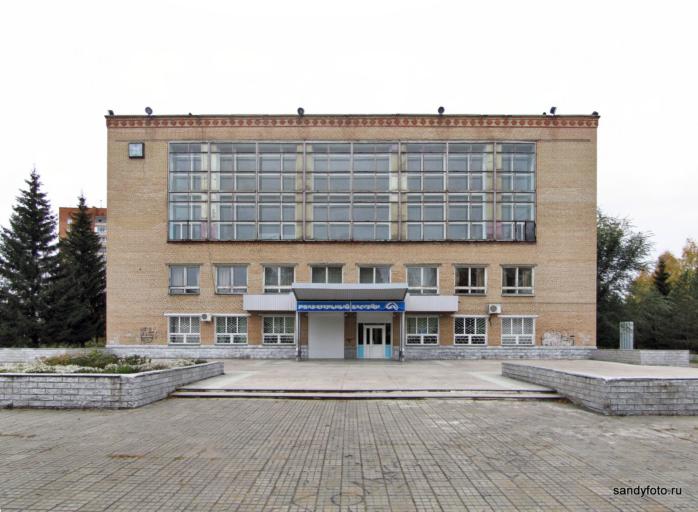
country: RU
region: Chelyabinsk
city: Troitsk
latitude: 54.0479
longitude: 61.6364
